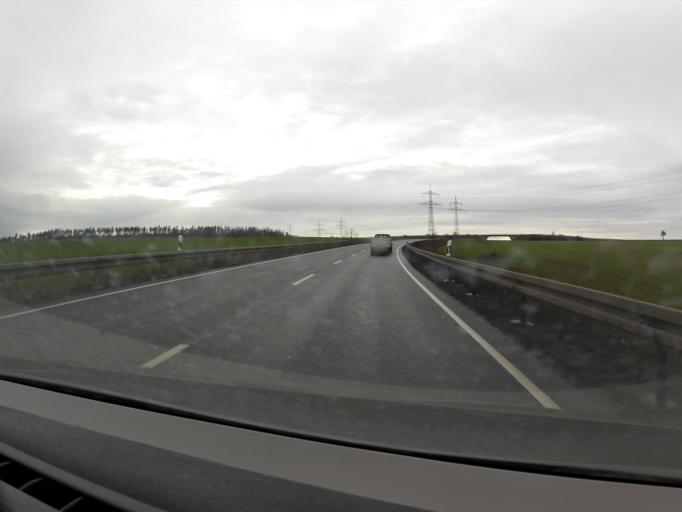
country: DE
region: Saxony-Anhalt
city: Grossorner
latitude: 51.6163
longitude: 11.4695
